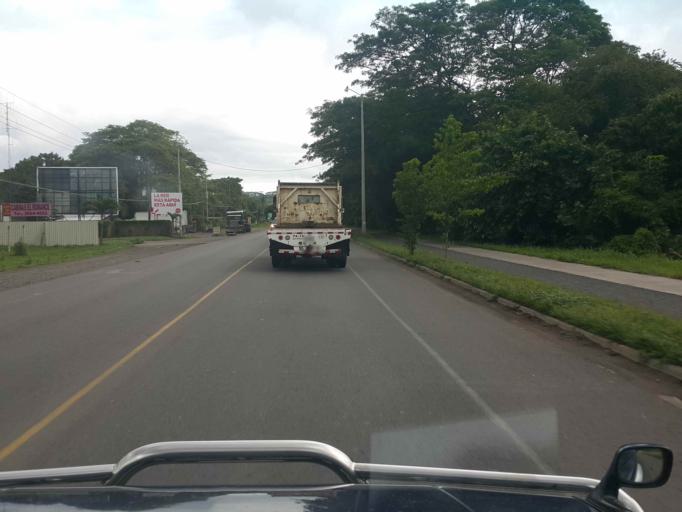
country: CR
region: Puntarenas
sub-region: Canton Central de Puntarenas
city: Chacarita
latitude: 9.9721
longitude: -84.7388
